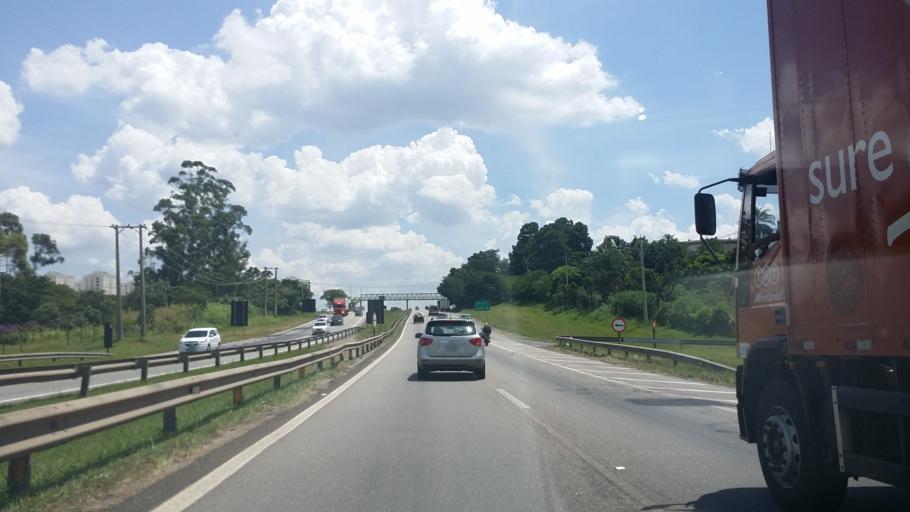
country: BR
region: Sao Paulo
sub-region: Jundiai
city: Jundiai
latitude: -23.1815
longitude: -46.9645
